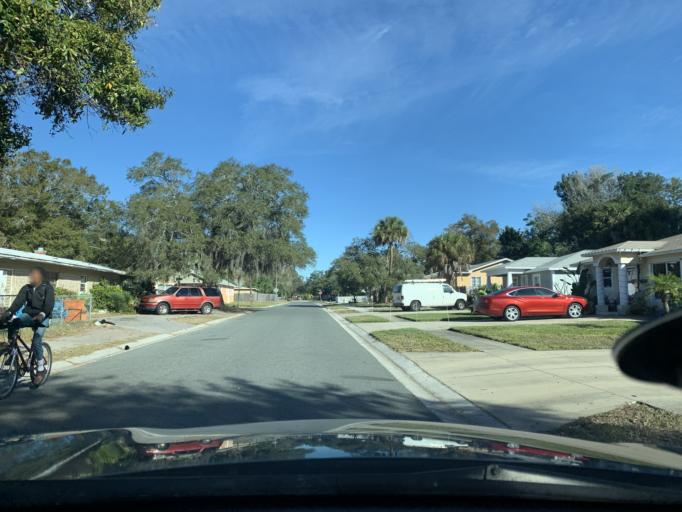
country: US
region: Florida
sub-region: Pinellas County
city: Gulfport
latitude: 27.7505
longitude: -82.6940
